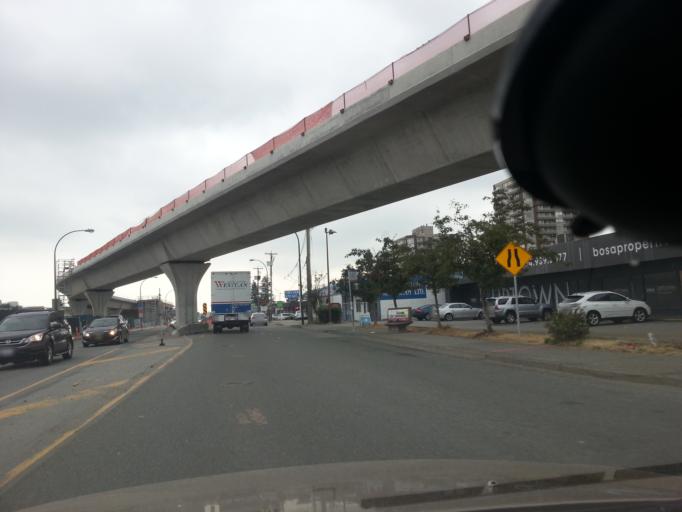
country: CA
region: British Columbia
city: Port Moody
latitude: 49.2630
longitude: -122.8882
